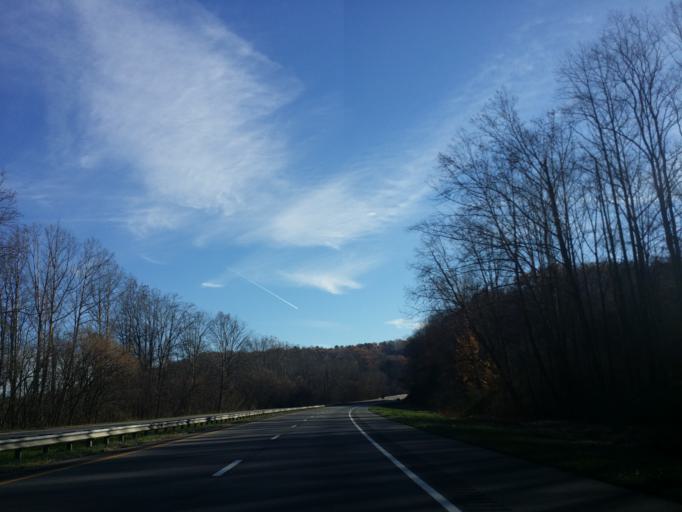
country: US
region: North Carolina
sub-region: McDowell County
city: West Marion
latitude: 35.6408
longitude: -82.1202
